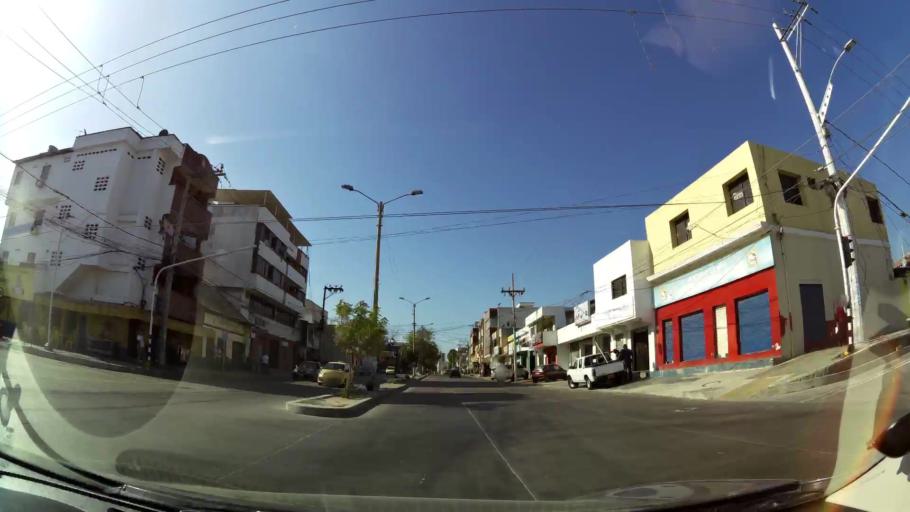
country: CO
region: Atlantico
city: Barranquilla
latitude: 10.9896
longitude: -74.7840
